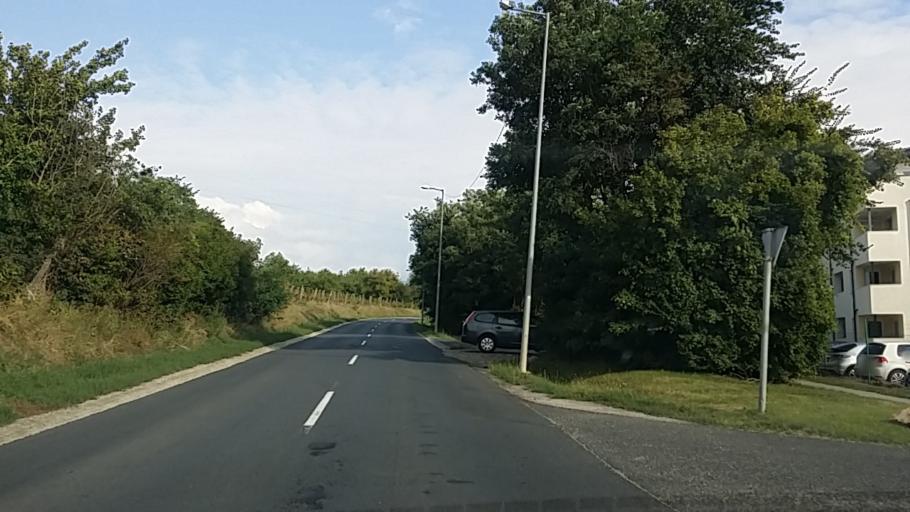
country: HU
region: Gyor-Moson-Sopron
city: Sopron
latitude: 47.6800
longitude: 16.6194
